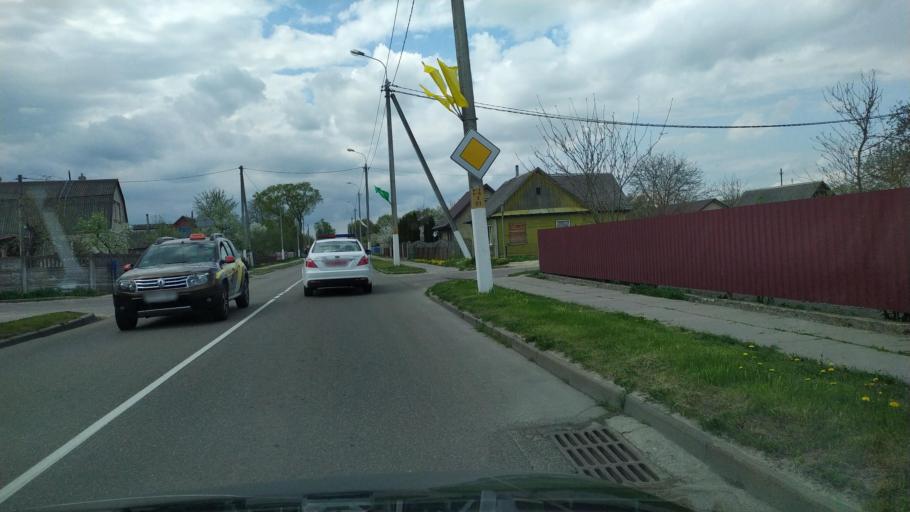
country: BY
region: Brest
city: Pruzhany
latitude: 52.5569
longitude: 24.4355
